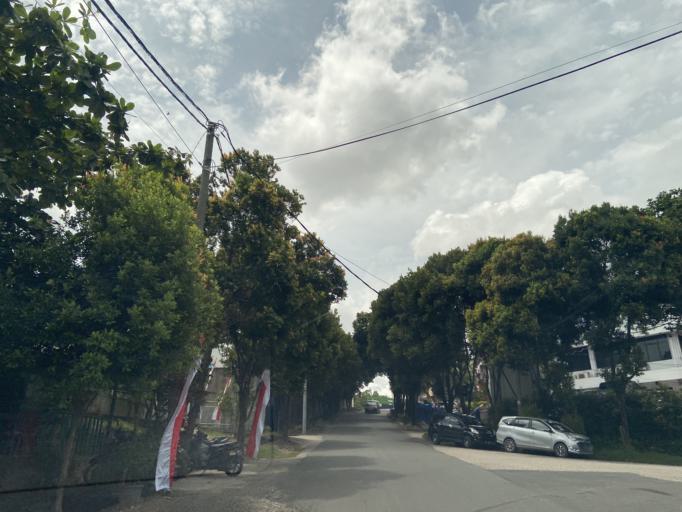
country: SG
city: Singapore
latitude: 1.1610
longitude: 104.0103
